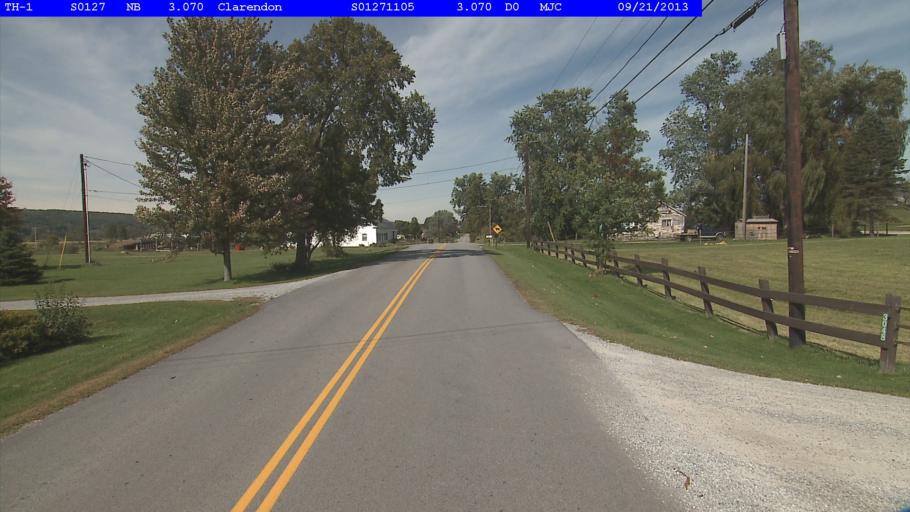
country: US
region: Vermont
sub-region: Rutland County
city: Rutland
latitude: 43.5576
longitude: -72.9716
